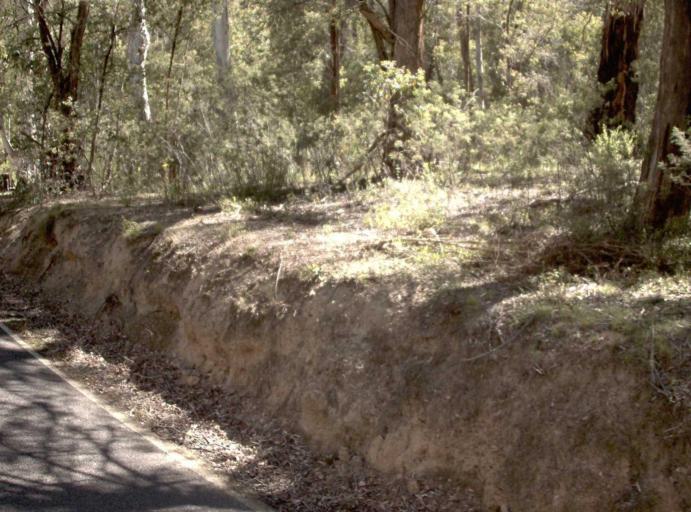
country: AU
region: New South Wales
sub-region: Bombala
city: Bombala
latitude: -37.1520
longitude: 148.7242
